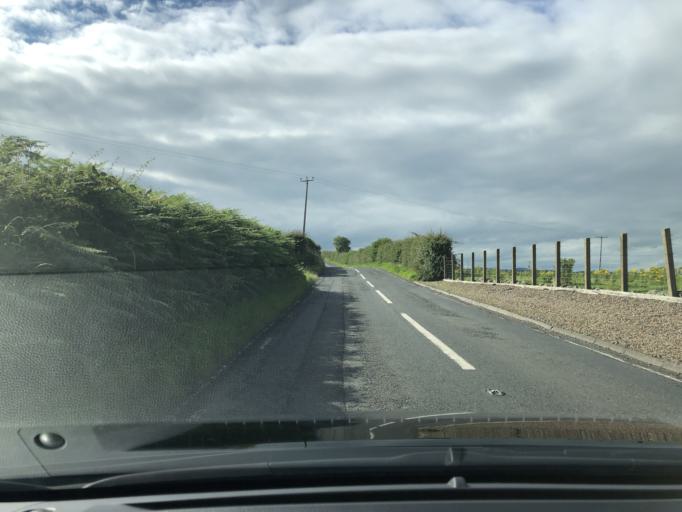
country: GB
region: Northern Ireland
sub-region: Down District
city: Dundrum
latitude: 54.2754
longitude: -5.7957
